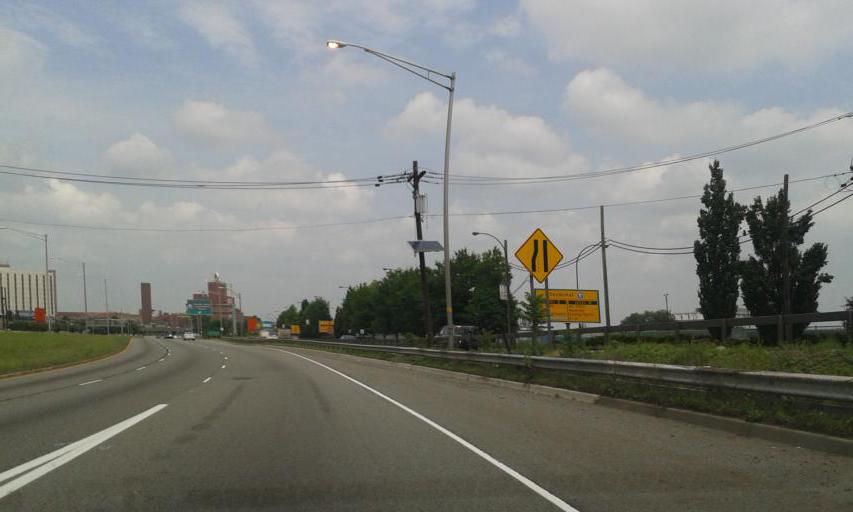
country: US
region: New Jersey
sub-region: Union County
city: Elizabeth
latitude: 40.6817
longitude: -74.1924
